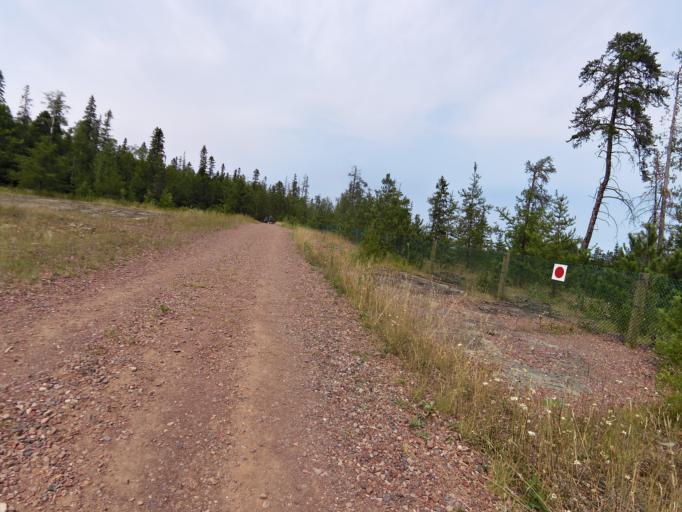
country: CA
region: Ontario
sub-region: Thunder Bay District
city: Thunder Bay
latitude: 48.8015
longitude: -88.6186
